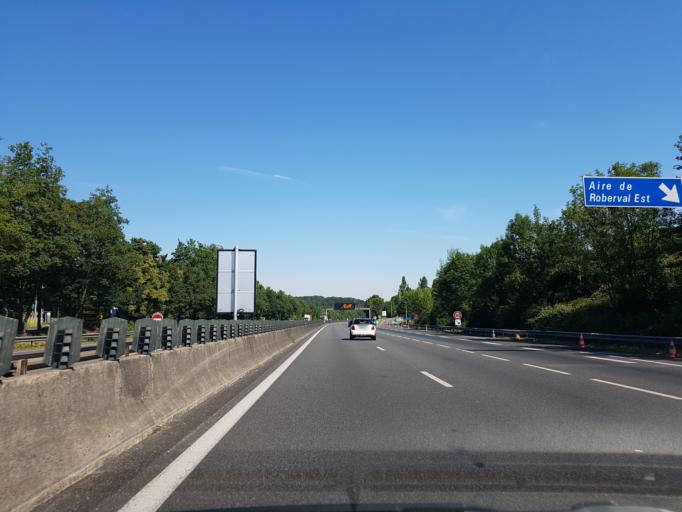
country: FR
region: Picardie
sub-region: Departement de l'Oise
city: Pontpoint
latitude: 49.2849
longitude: 2.6937
